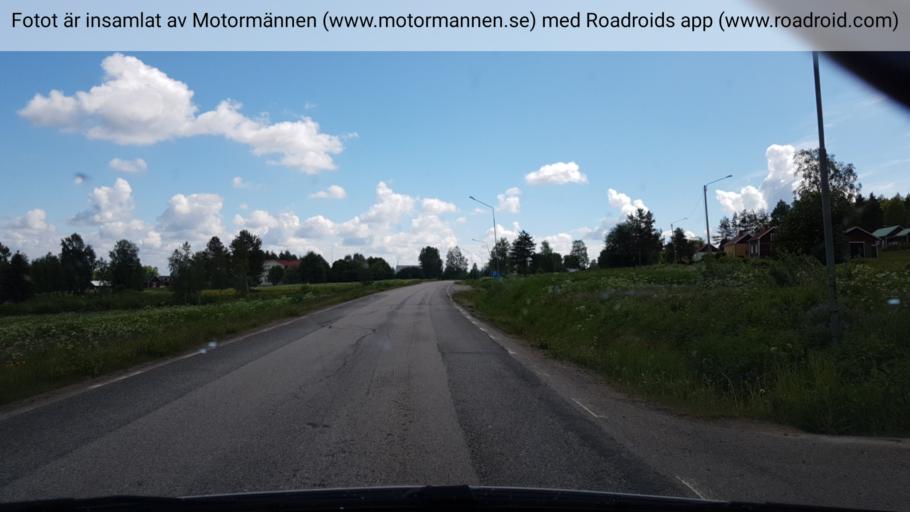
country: FI
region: Lapland
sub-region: Torniolaakso
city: Ylitornio
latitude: 66.1752
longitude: 23.8023
